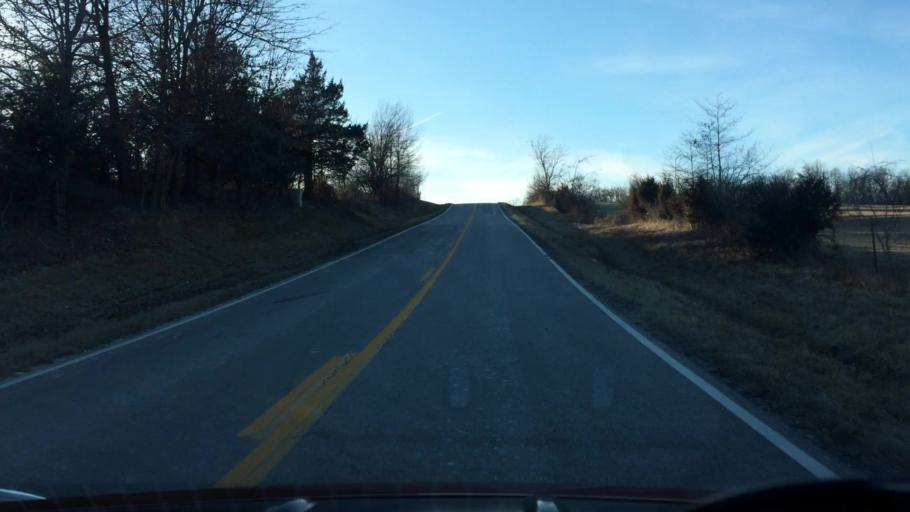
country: US
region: Missouri
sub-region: Webster County
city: Marshfield
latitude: 37.3408
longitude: -92.9717
